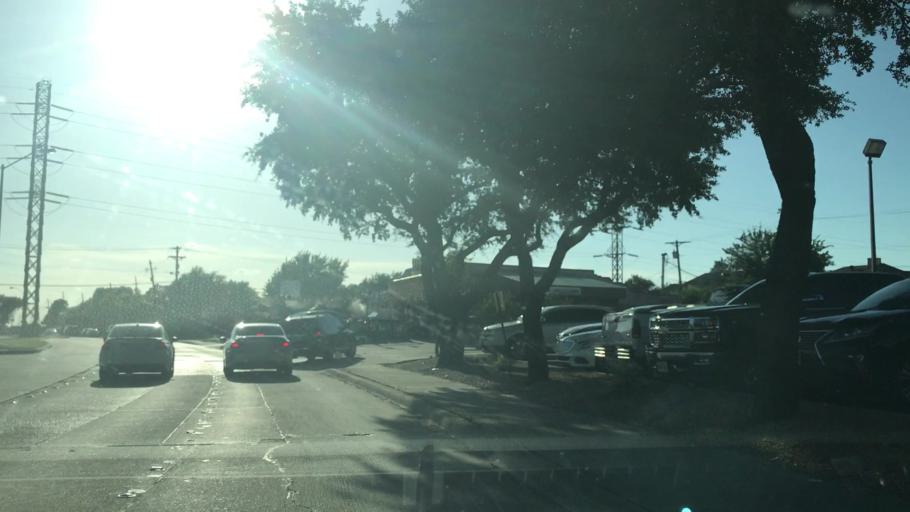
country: US
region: Texas
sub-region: Collin County
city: Plano
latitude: 33.0408
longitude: -96.7088
